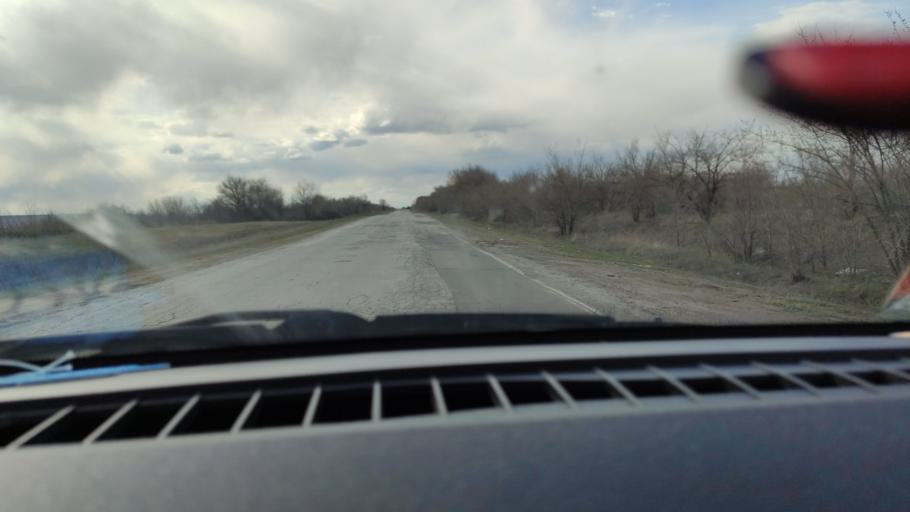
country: RU
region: Saratov
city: Rovnoye
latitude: 51.0408
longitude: 46.0686
